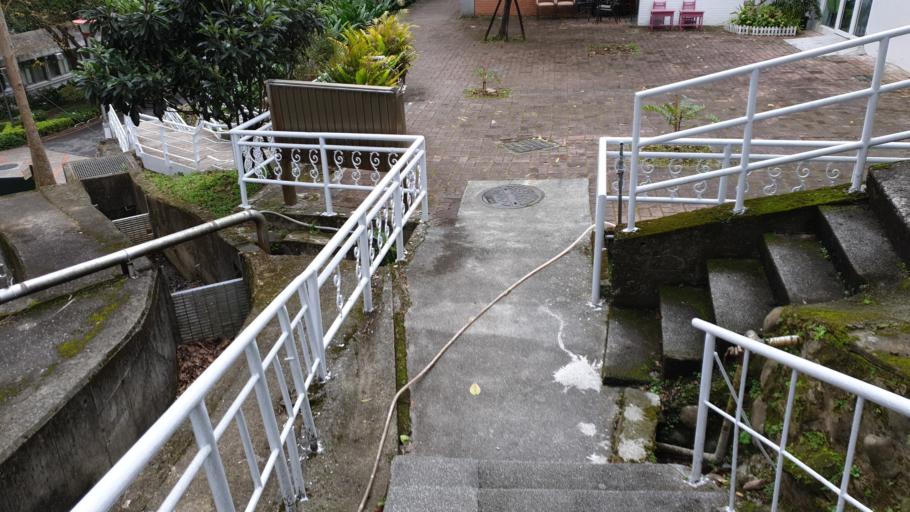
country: TW
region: Taipei
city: Taipei
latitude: 25.0927
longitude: 121.5466
